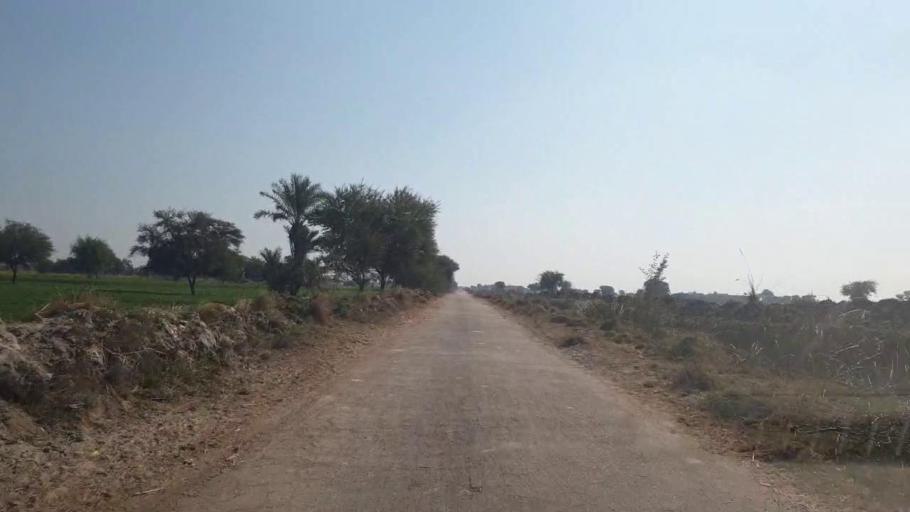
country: PK
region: Sindh
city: Shahdadpur
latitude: 25.9626
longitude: 68.6214
